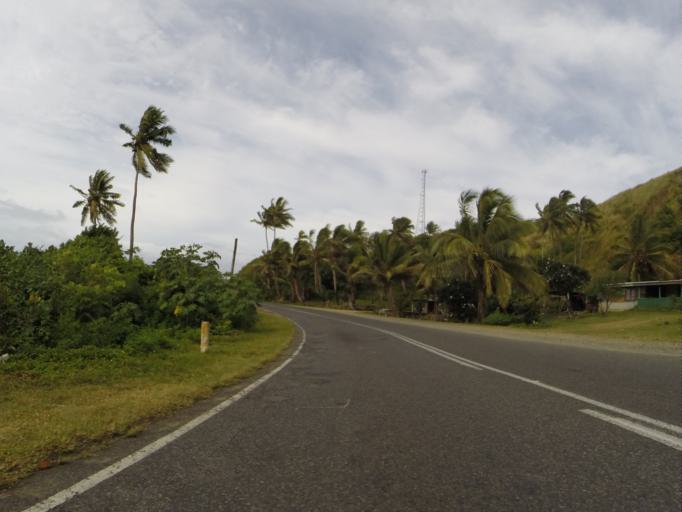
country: FJ
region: Western
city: Nadi
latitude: -18.1796
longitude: 177.5860
